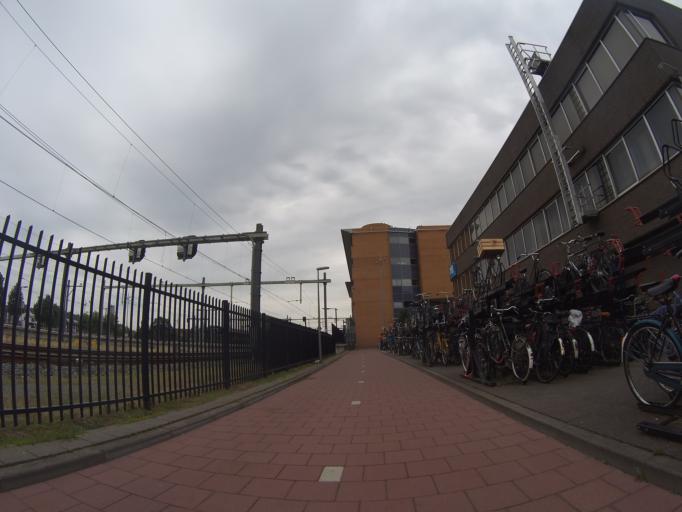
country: NL
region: North Holland
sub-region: Gemeente Hilversum
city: Hilversum
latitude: 52.2275
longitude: 5.1805
